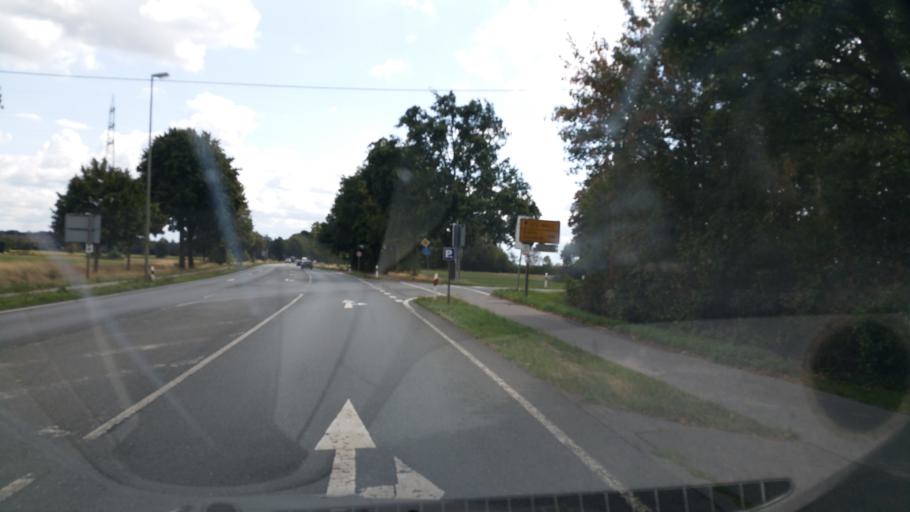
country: DE
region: North Rhine-Westphalia
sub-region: Regierungsbezirk Dusseldorf
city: Hamminkeln
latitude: 51.7206
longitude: 6.5948
